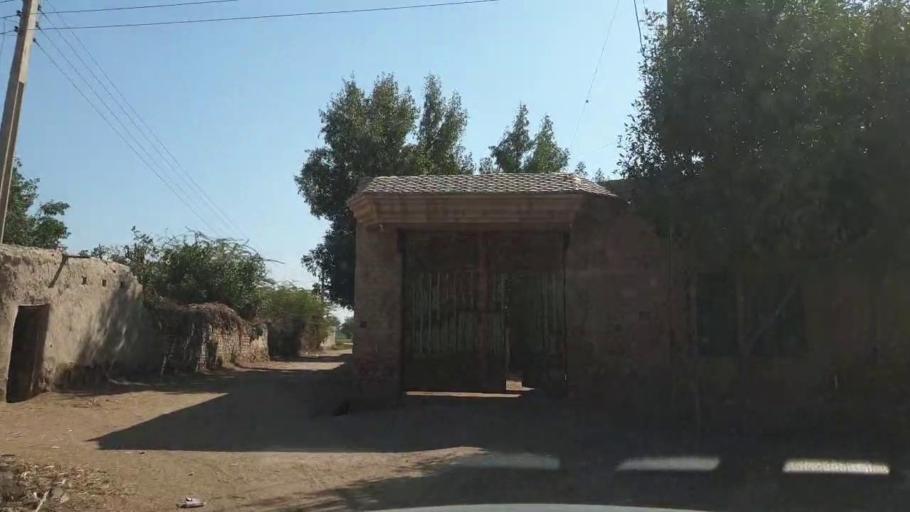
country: PK
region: Sindh
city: Tando Adam
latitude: 25.6507
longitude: 68.6985
